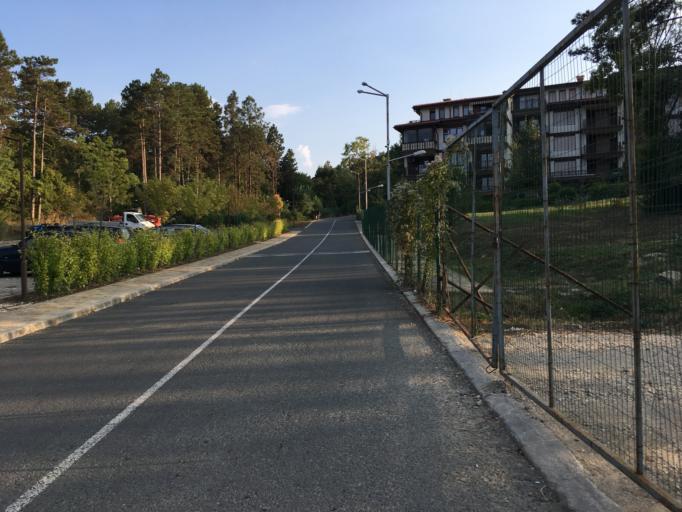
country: BG
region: Burgas
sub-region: Obshtina Sozopol
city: Sozopol
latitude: 42.4117
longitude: 27.6829
